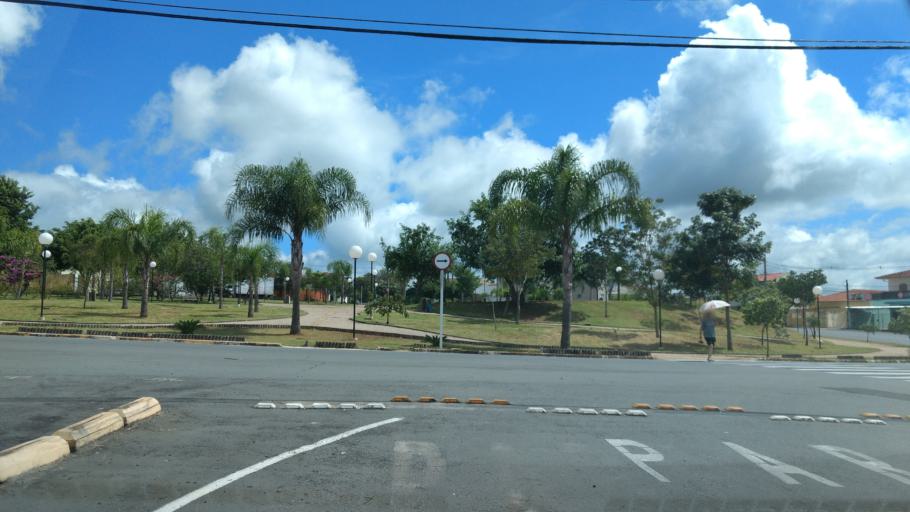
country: BR
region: Sao Paulo
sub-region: Botucatu
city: Botucatu
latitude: -22.8601
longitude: -48.4414
